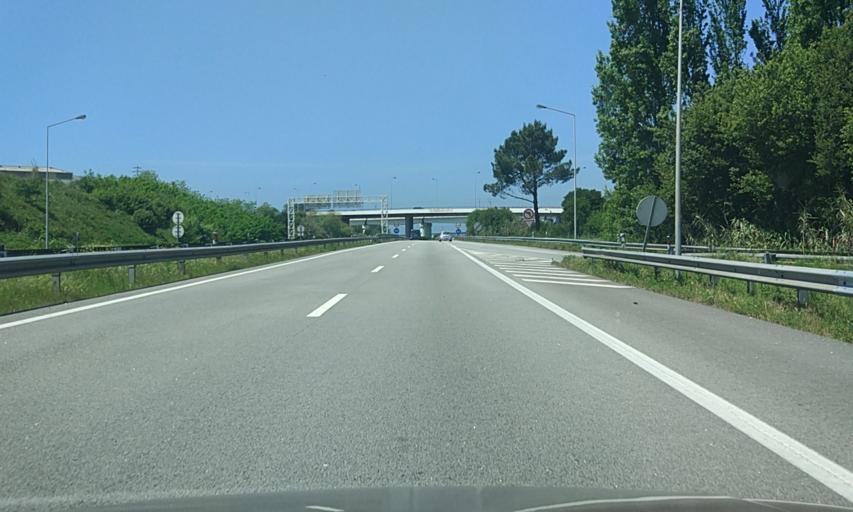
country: PT
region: Aveiro
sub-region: Aveiro
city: Aveiro
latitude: 40.6503
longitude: -8.6255
